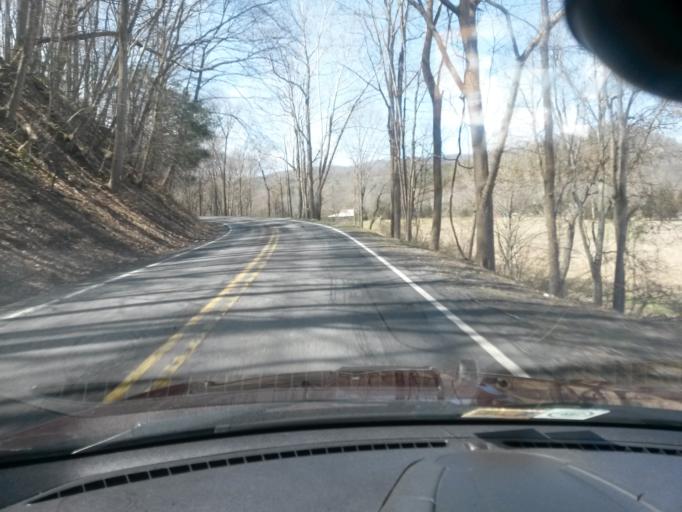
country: US
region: Virginia
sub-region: City of Covington
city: Covington
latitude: 37.7569
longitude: -80.1374
